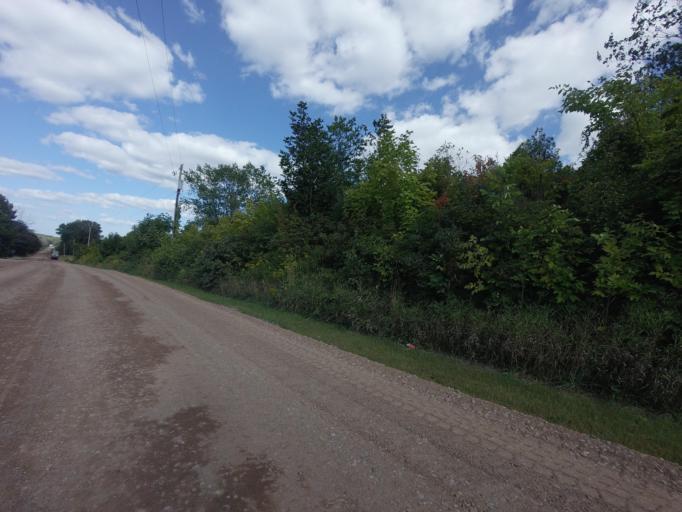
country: CA
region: Ontario
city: Orangeville
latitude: 43.8073
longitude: -79.9573
